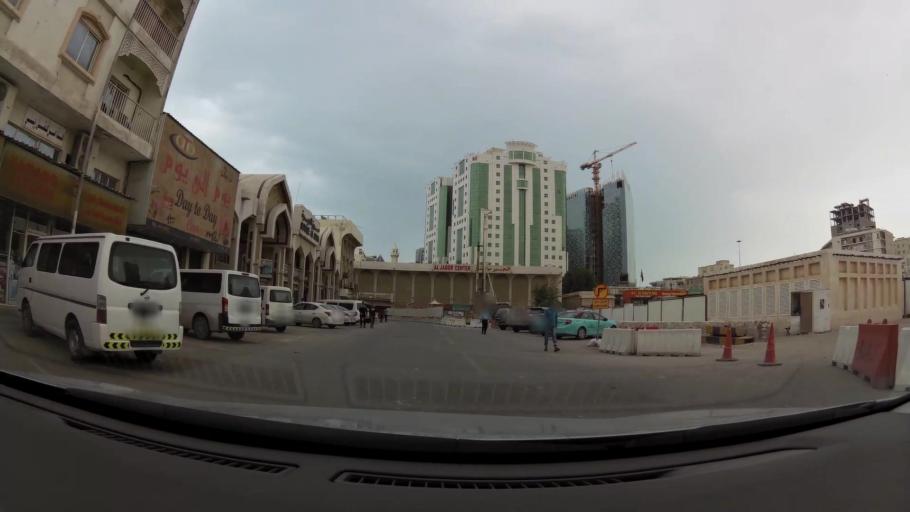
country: QA
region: Baladiyat ad Dawhah
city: Doha
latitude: 25.2877
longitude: 51.5383
